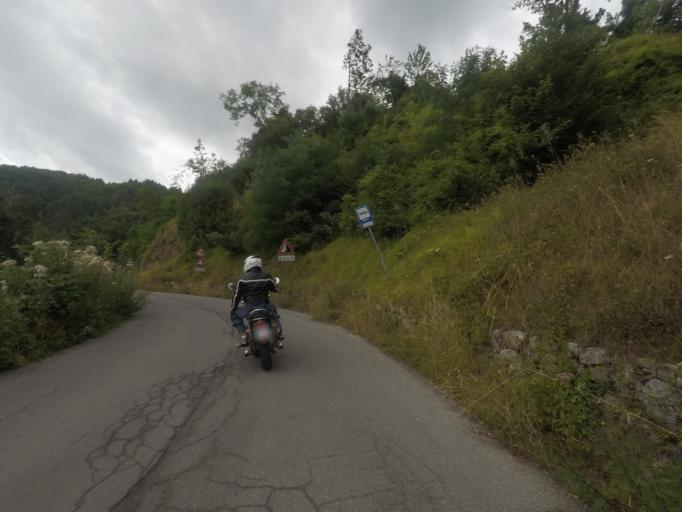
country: IT
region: Tuscany
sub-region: Provincia di Lucca
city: Careggine
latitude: 44.1130
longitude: 10.3646
